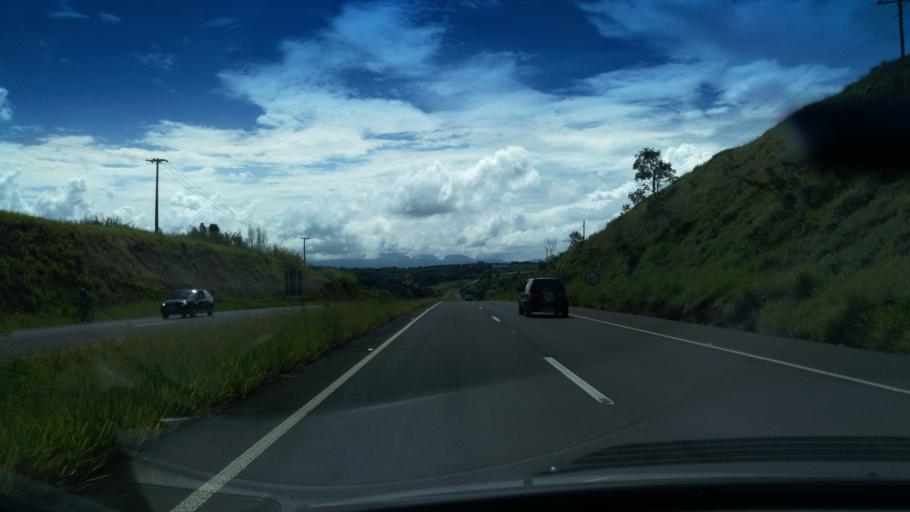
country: BR
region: Sao Paulo
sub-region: Santo Antonio Do Jardim
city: Espirito Santo do Pinhal
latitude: -22.1701
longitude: -46.7425
